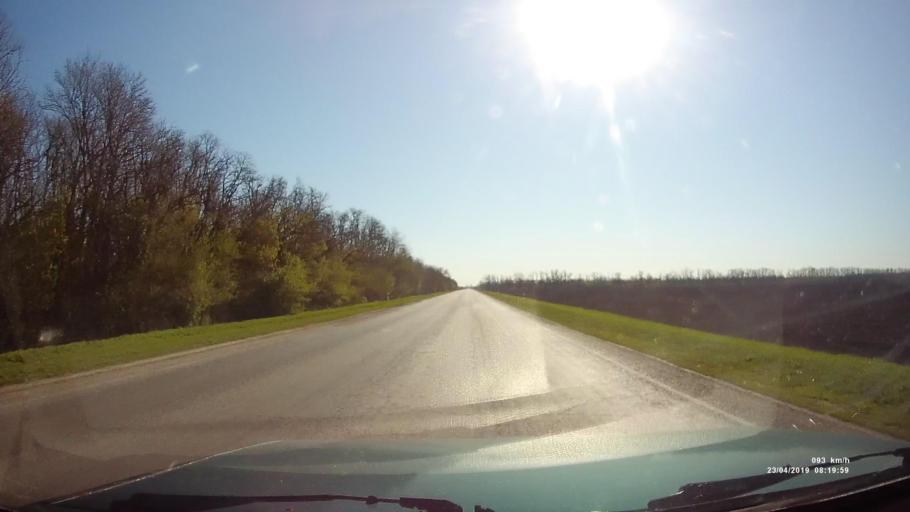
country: RU
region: Rostov
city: Tselina
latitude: 46.5373
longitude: 40.8607
